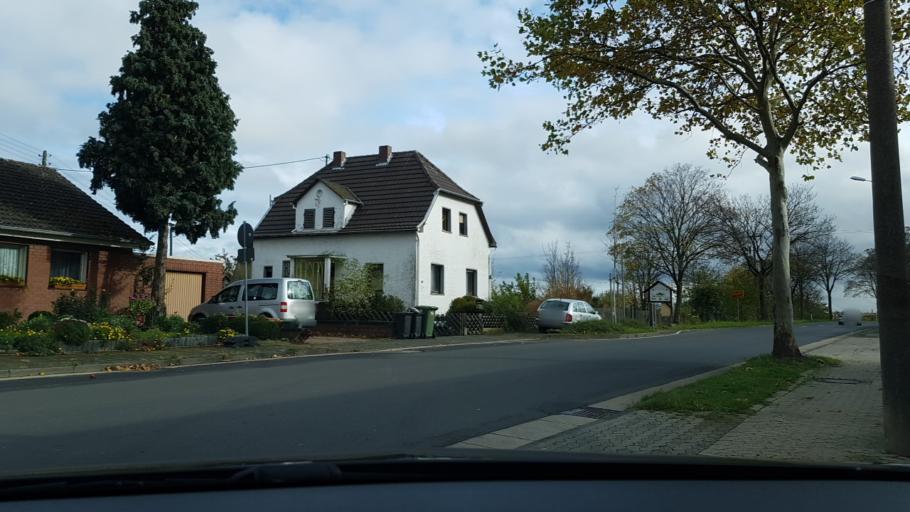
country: DE
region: North Rhine-Westphalia
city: Meckenheim
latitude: 50.6043
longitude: 6.9938
